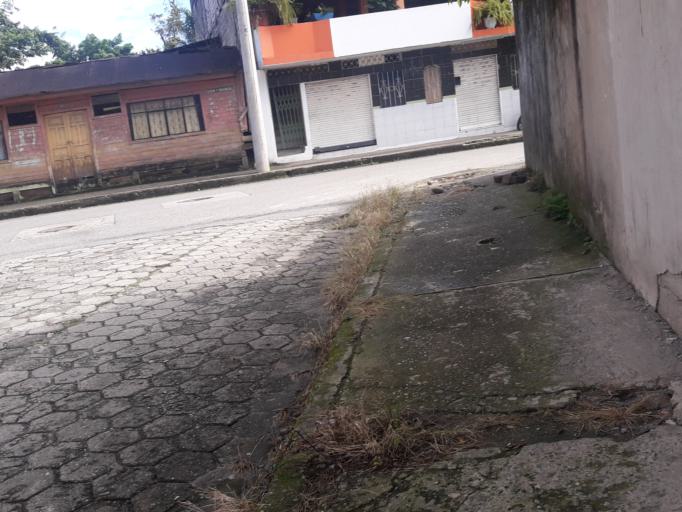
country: EC
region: Napo
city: Tena
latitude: -0.9871
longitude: -77.8125
